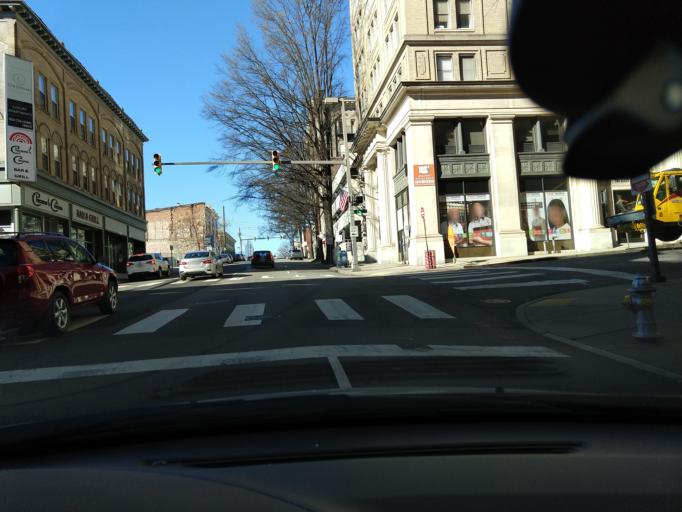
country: US
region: Virginia
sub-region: City of Richmond
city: Richmond
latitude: 37.5398
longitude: -77.4388
